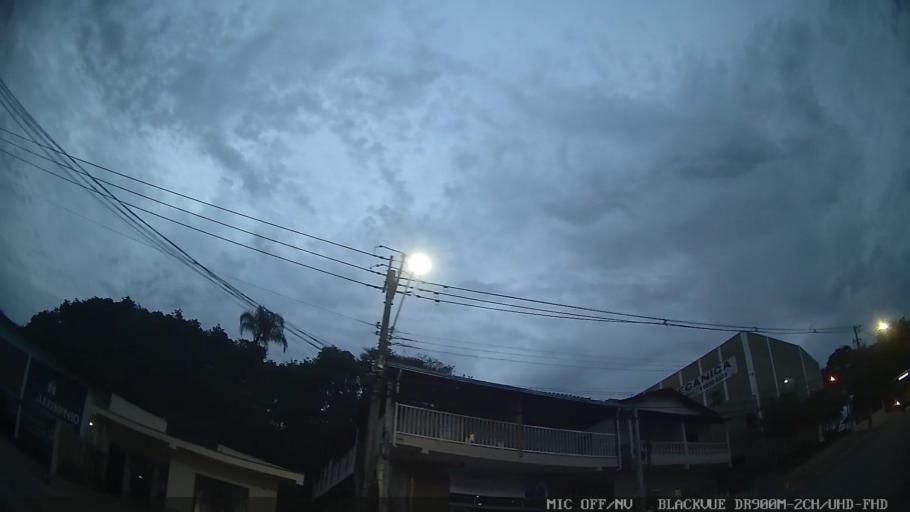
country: BR
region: Sao Paulo
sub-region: Itatiba
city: Itatiba
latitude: -22.8780
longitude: -46.7939
